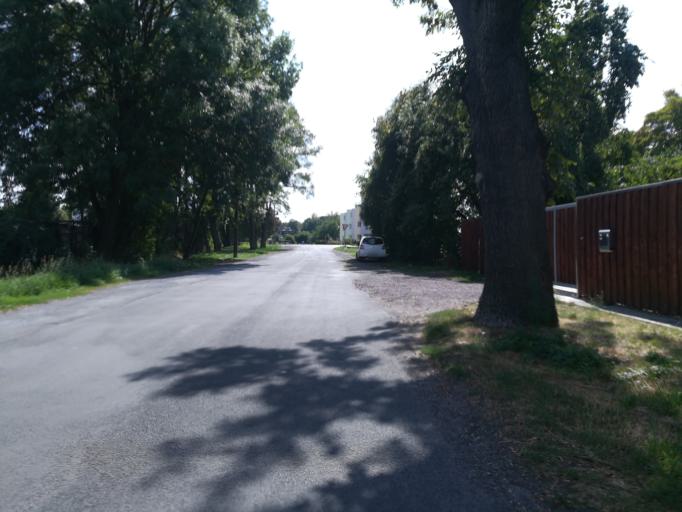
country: DE
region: Saxony-Anhalt
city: Neue Neustadt
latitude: 52.1451
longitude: 11.6111
